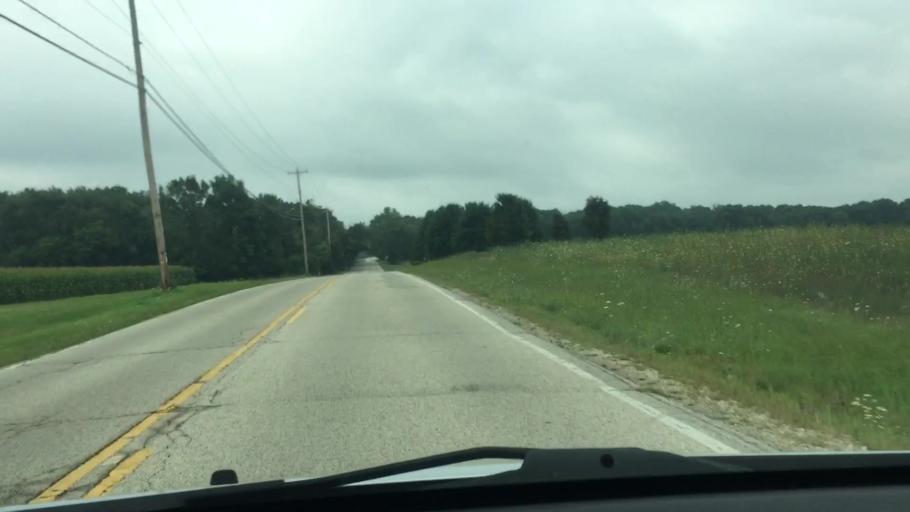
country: US
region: Wisconsin
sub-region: Waukesha County
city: Delafield
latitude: 43.0443
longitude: -88.4425
